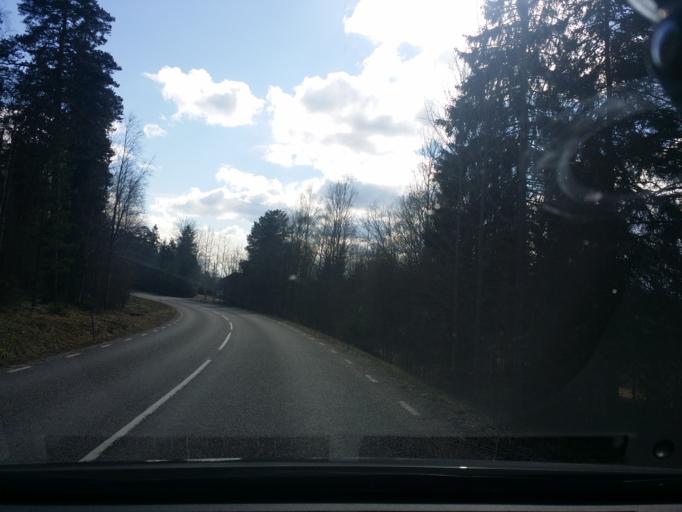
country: SE
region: Vaestmanland
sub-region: Sala Kommun
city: Sala
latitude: 59.9897
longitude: 16.4771
